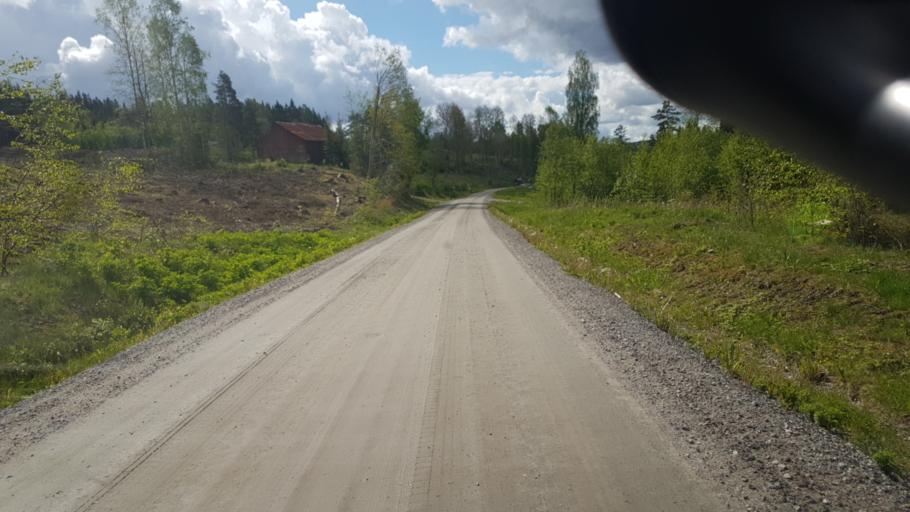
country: NO
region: Ostfold
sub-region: Romskog
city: Romskog
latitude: 59.6797
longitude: 11.9334
